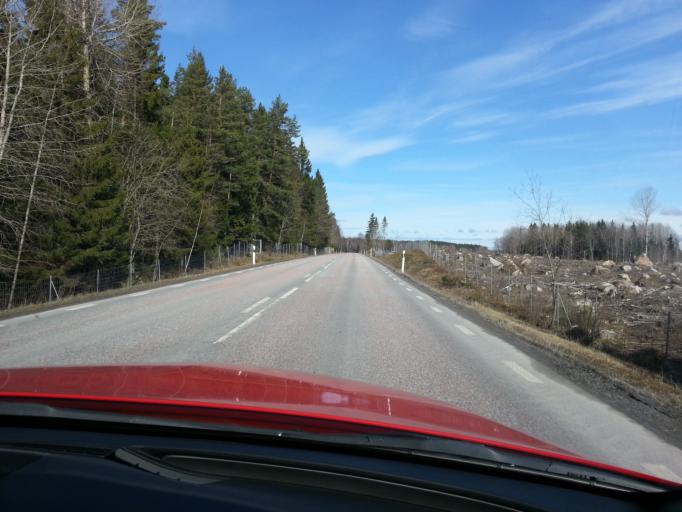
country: SE
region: Uppsala
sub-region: Osthammars Kommun
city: Gimo
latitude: 60.1418
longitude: 18.1579
